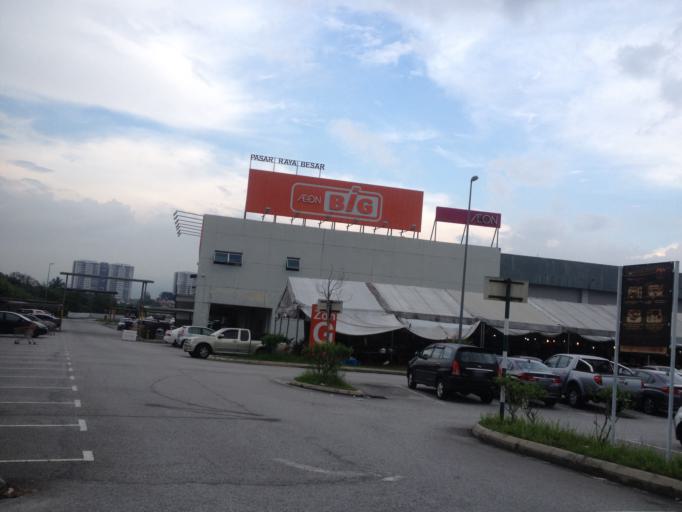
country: MY
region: Selangor
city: Kampong Baharu Balakong
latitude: 3.0482
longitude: 101.7579
